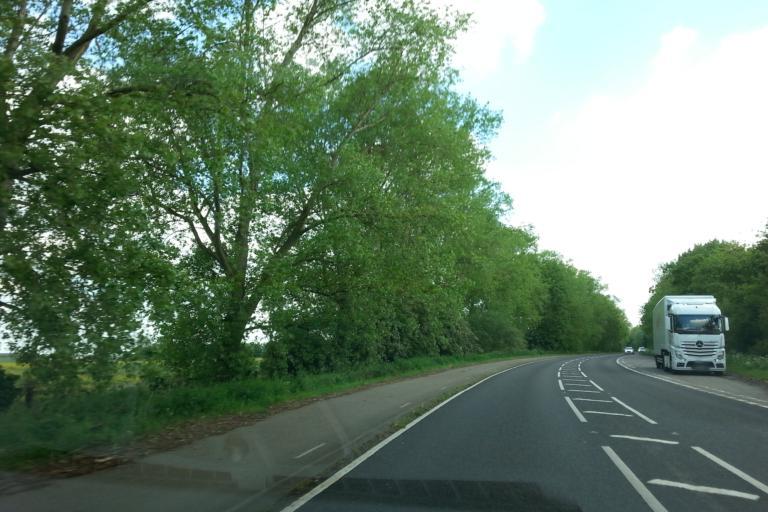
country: GB
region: England
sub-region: Cambridgeshire
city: Yaxley
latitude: 52.5090
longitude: -0.2798
